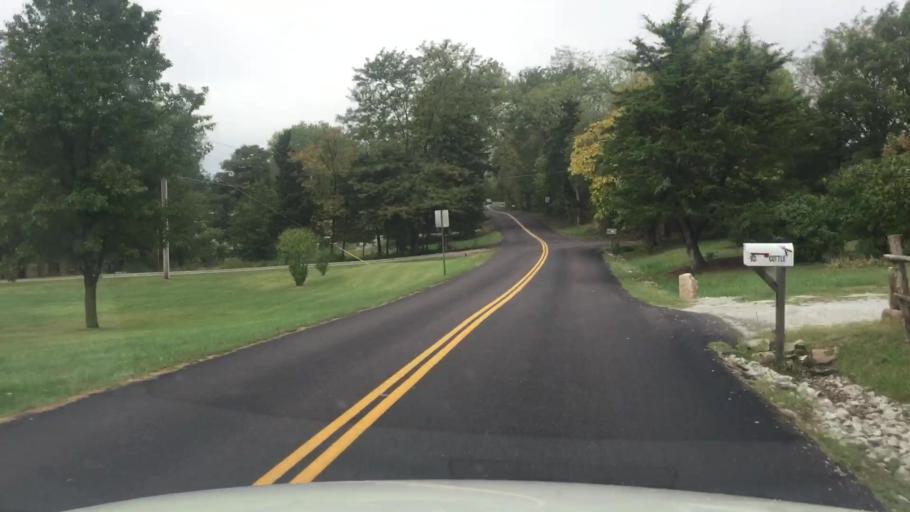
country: US
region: Missouri
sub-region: Boone County
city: Columbia
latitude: 38.8605
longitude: -92.3315
